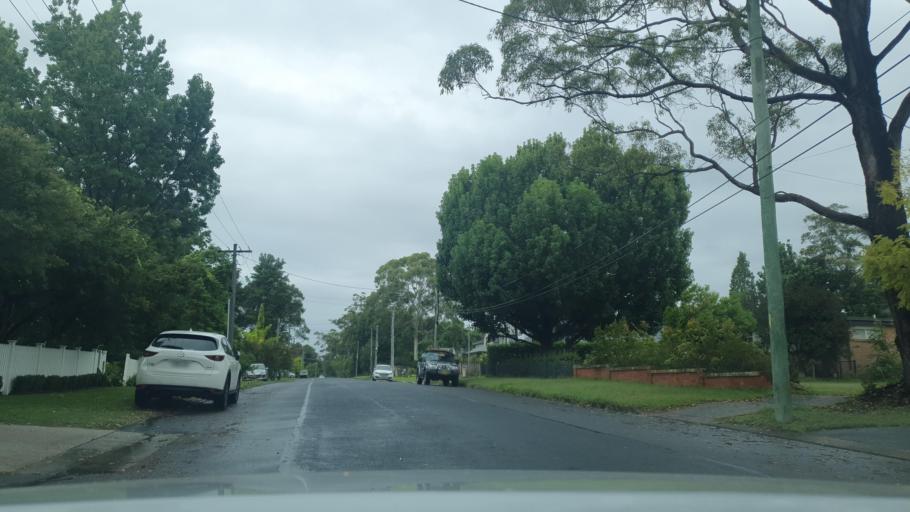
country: AU
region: New South Wales
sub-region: Blue Mountains Municipality
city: Glenbrook
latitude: -33.7726
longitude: 150.6288
